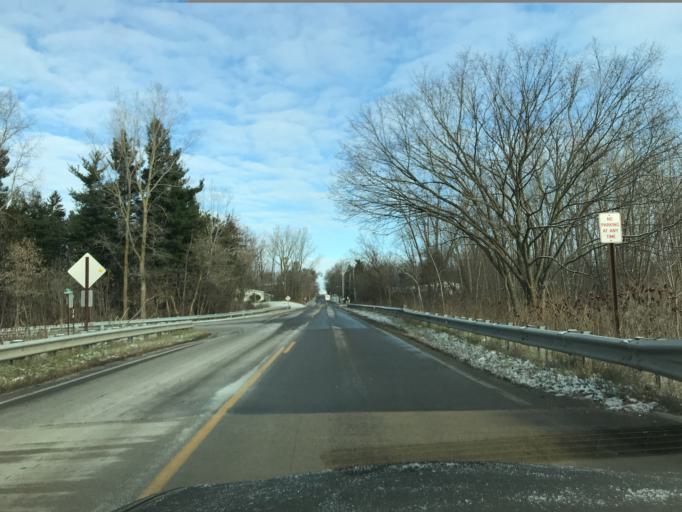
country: US
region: Michigan
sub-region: Eaton County
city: Dimondale
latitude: 42.6711
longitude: -84.6423
